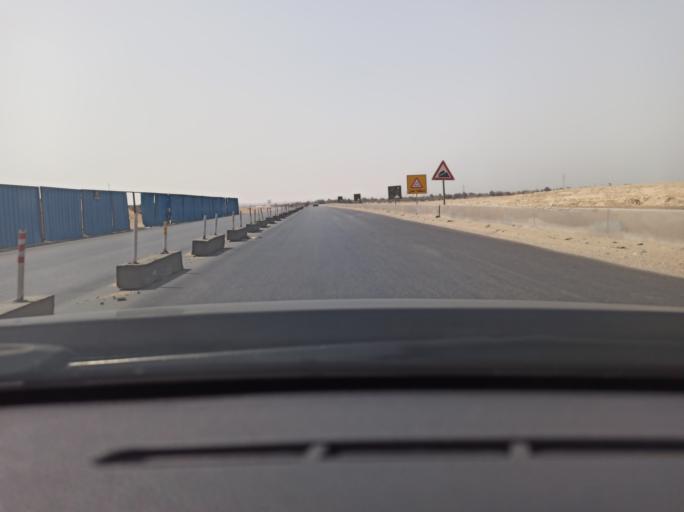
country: EG
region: Muhafazat al Fayyum
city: Al Wasitah
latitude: 29.2813
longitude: 31.2681
